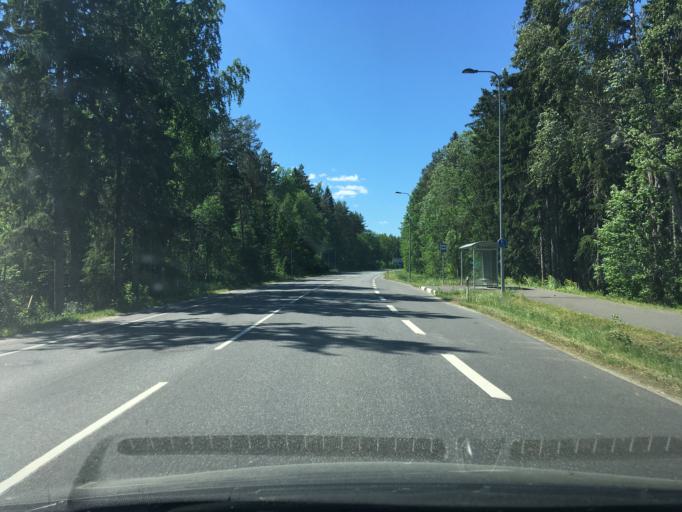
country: EE
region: Harju
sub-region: Rae vald
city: Vaida
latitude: 59.1899
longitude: 25.0433
